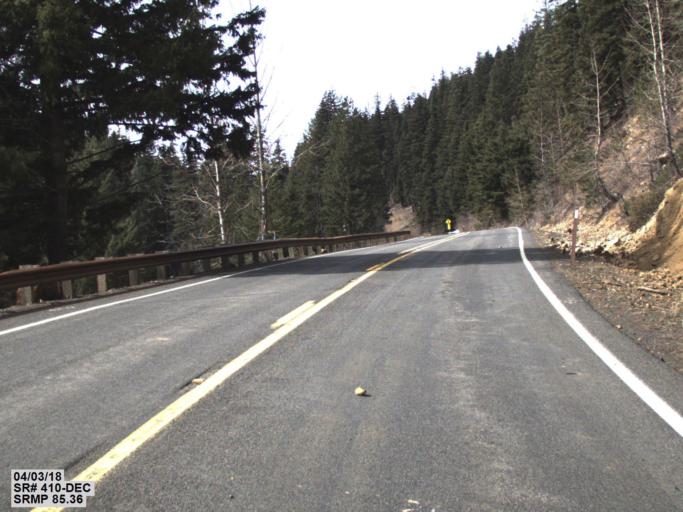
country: US
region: Washington
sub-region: Kittitas County
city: Cle Elum
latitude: 46.9678
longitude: -121.2278
